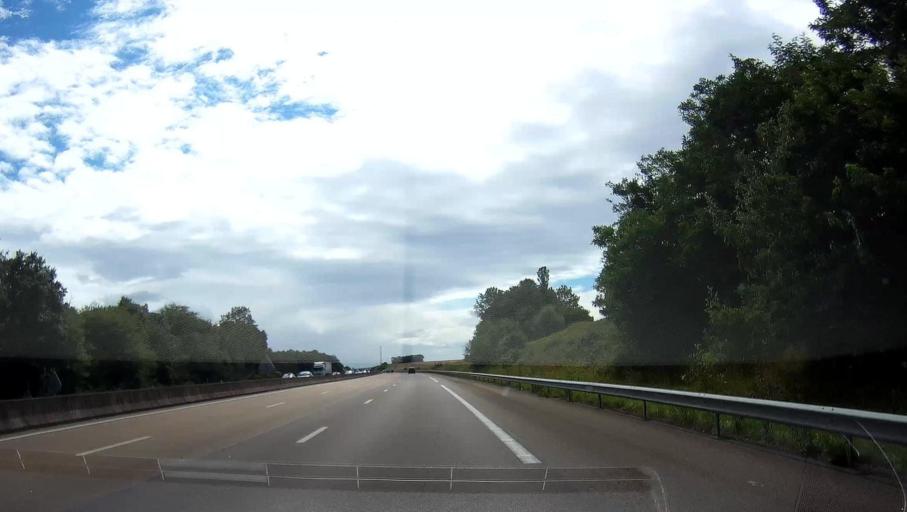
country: FR
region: Bourgogne
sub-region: Departement de la Cote-d'Or
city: Saint-Julien
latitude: 47.4623
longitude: 5.1790
